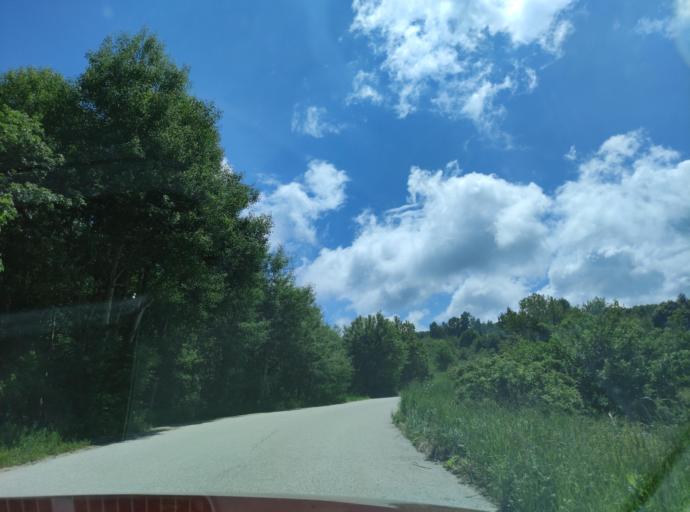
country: BG
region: Sofia-Capital
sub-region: Stolichna Obshtina
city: Sofia
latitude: 42.6346
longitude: 23.2340
